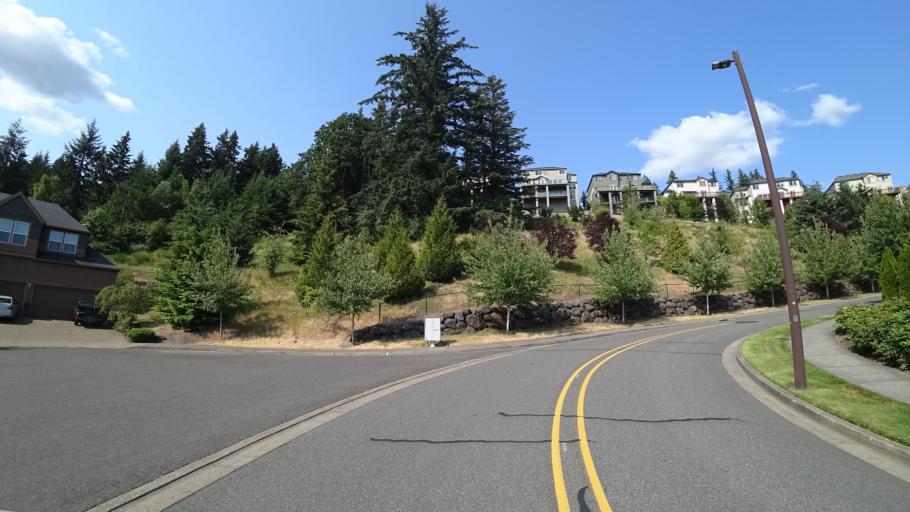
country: US
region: Oregon
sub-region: Clackamas County
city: Happy Valley
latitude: 45.4426
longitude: -122.5519
